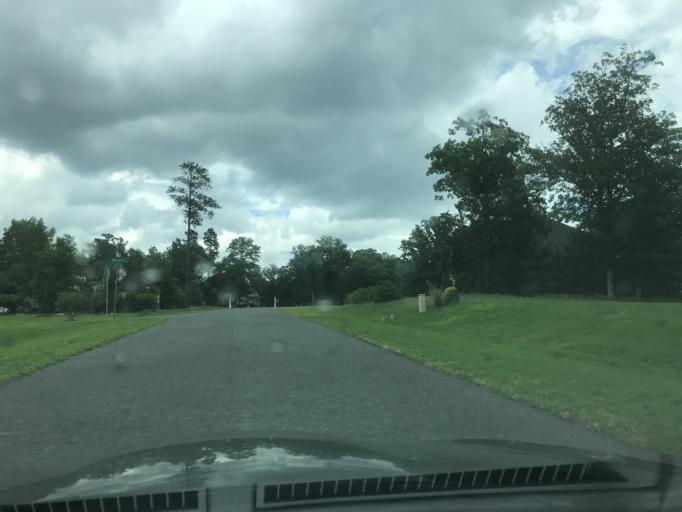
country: US
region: North Carolina
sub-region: Wake County
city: Knightdale
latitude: 35.8347
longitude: -78.4669
